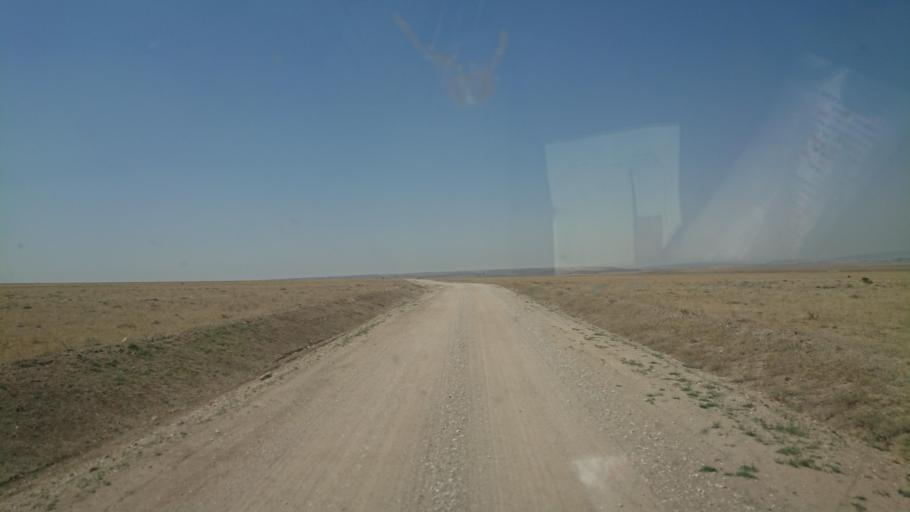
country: TR
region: Aksaray
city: Agacoren
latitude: 38.7443
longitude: 33.8926
